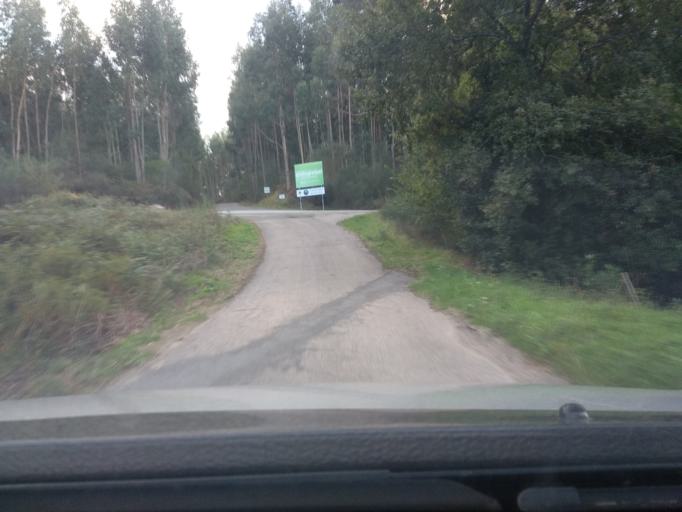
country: ES
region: Galicia
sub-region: Provincia de Pontevedra
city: Moana
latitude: 42.3042
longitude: -8.6955
